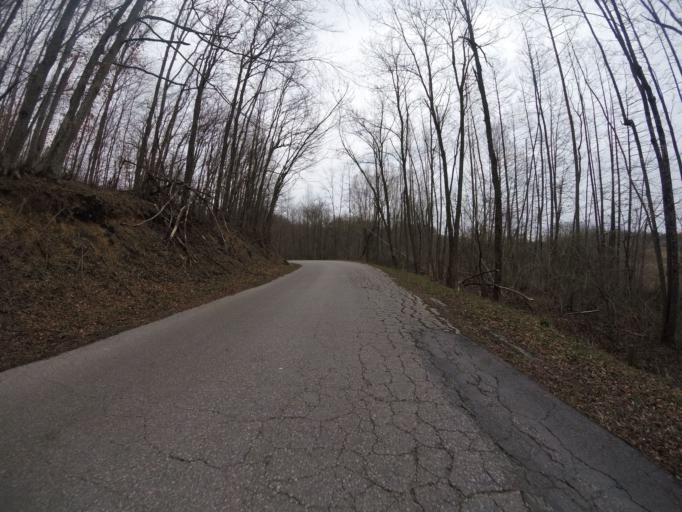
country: HR
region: Zagrebacka
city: Lukavec
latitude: 45.5588
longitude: 15.9793
